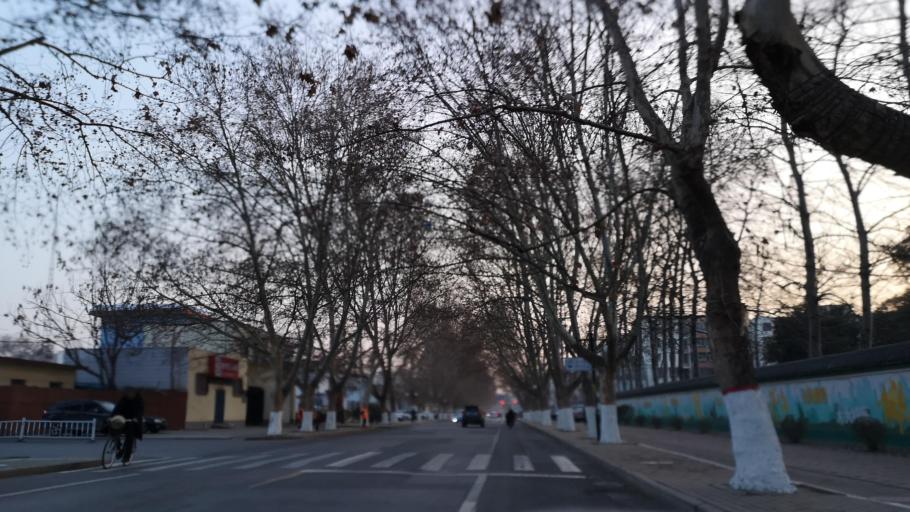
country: CN
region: Henan Sheng
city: Zhongyuanlu
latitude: 35.7712
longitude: 115.0750
